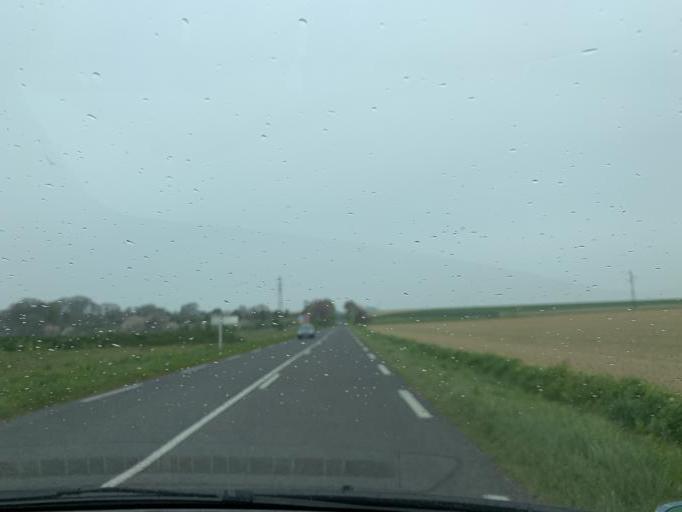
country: FR
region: Haute-Normandie
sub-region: Departement de la Seine-Maritime
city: Cany-Barville
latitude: 49.8046
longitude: 0.6667
